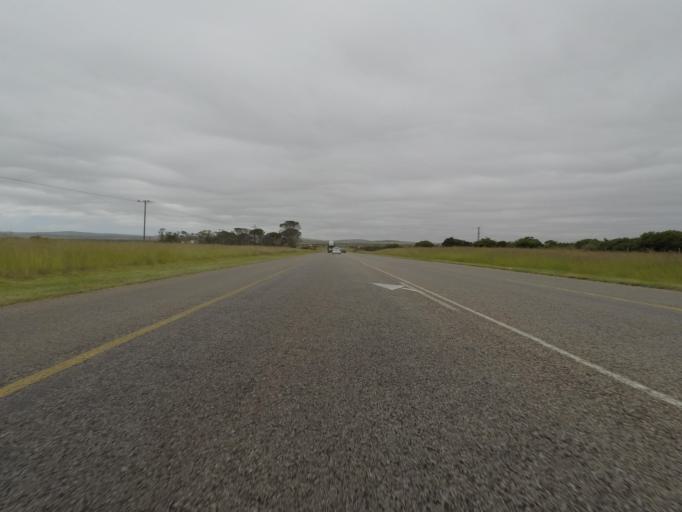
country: ZA
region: Eastern Cape
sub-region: Nelson Mandela Bay Metropolitan Municipality
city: Port Elizabeth
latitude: -33.6666
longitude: 25.8571
